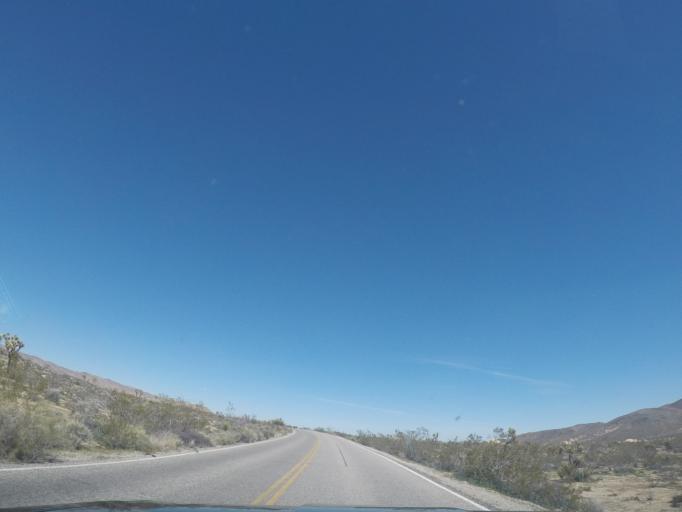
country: US
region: California
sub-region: San Bernardino County
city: Twentynine Palms
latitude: 33.9917
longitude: -116.0220
